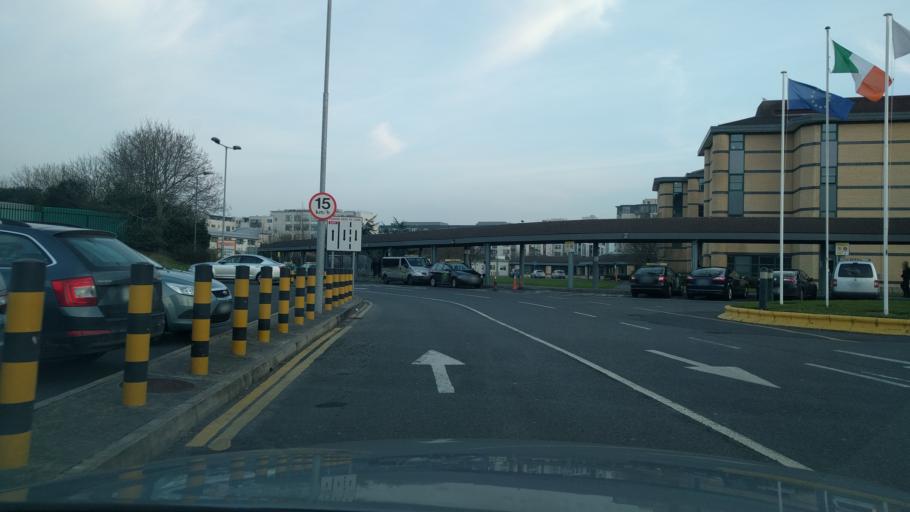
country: IE
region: Leinster
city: Tallaght
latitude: 53.2914
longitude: -6.3773
